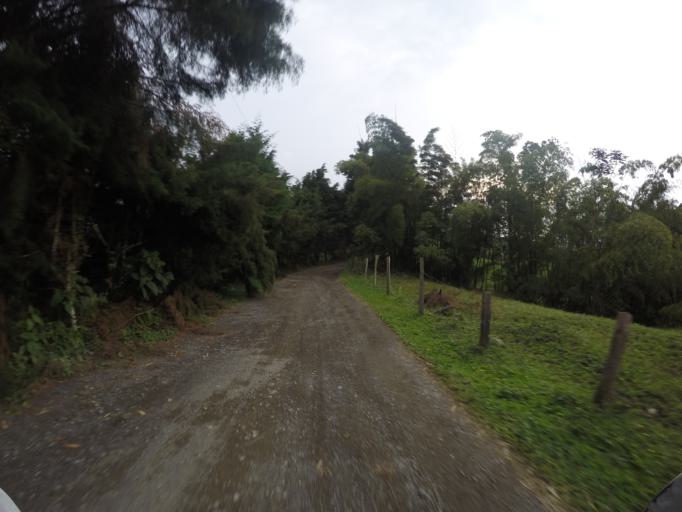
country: CO
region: Quindio
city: Filandia
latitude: 4.7125
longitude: -75.6402
